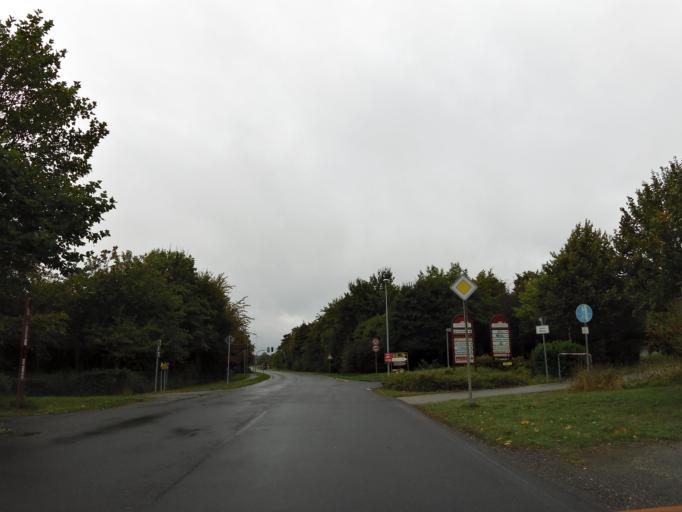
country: DE
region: Rheinland-Pfalz
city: Kastellaun
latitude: 50.0702
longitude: 7.4517
